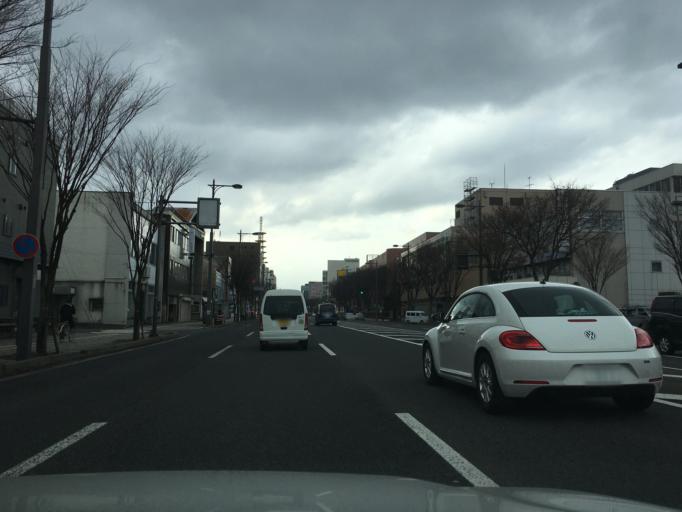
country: JP
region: Aomori
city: Aomori Shi
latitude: 40.8240
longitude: 140.7594
